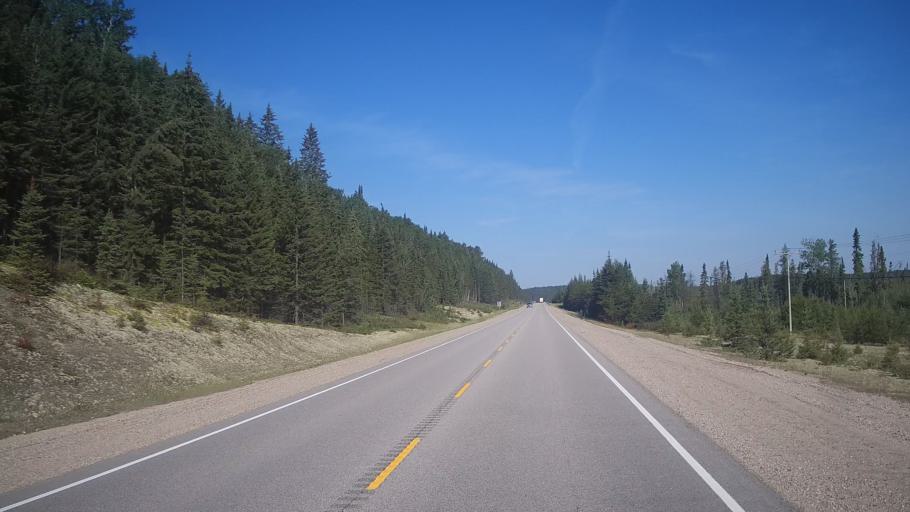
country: CA
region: Ontario
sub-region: Rainy River District
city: Atikokan
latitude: 49.4668
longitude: -91.9149
